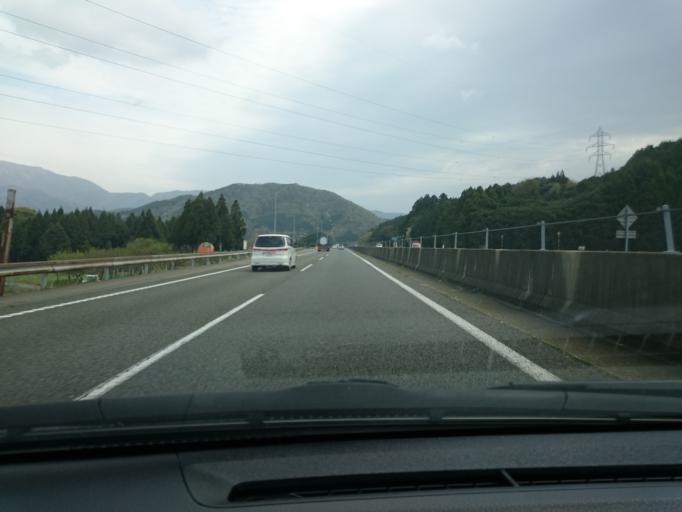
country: JP
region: Gifu
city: Tarui
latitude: 35.3377
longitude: 136.4040
